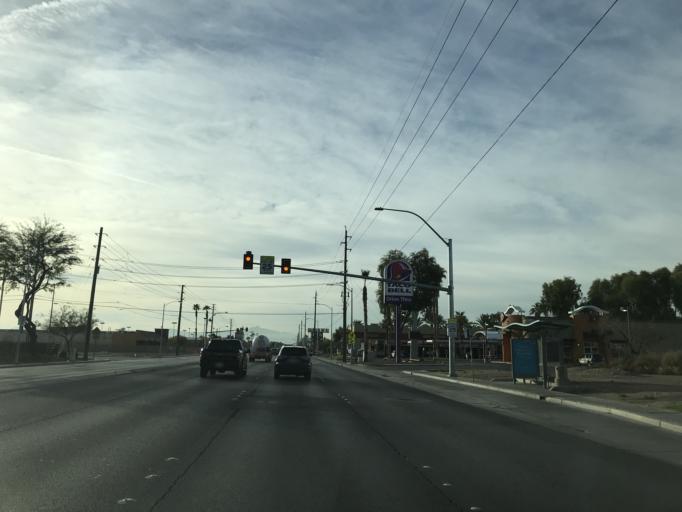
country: US
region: Nevada
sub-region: Clark County
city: Sunrise Manor
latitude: 36.1711
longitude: -115.0622
